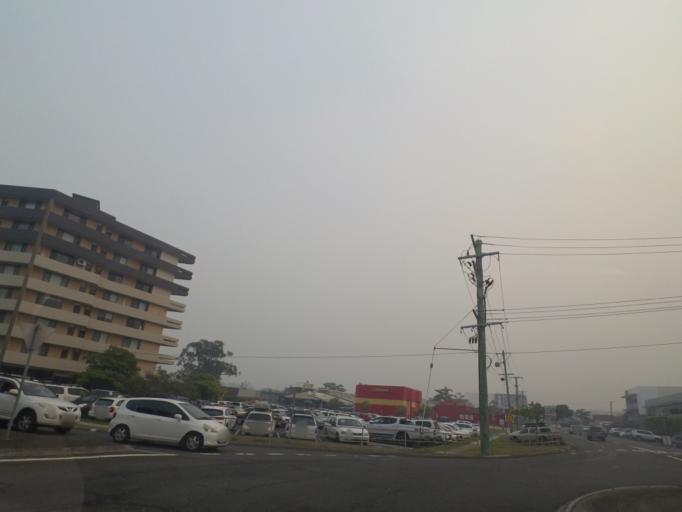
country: AU
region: New South Wales
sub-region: Coffs Harbour
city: Coffs Harbour
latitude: -30.2998
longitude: 153.1145
